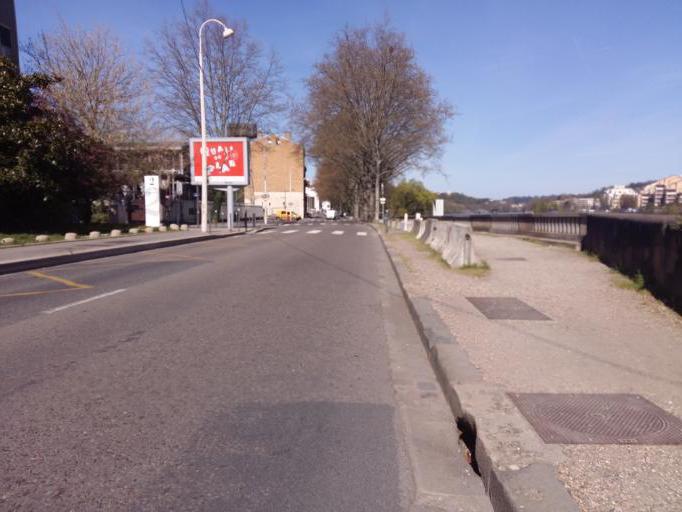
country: FR
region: Rhone-Alpes
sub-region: Departement du Rhone
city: Caluire-et-Cuire
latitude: 45.7846
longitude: 4.8126
